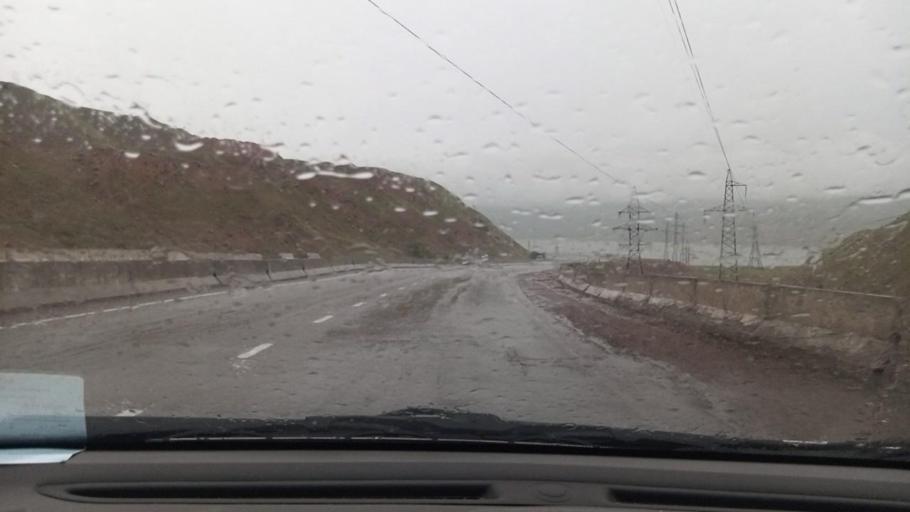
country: UZ
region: Toshkent
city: Angren
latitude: 41.0602
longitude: 70.1915
